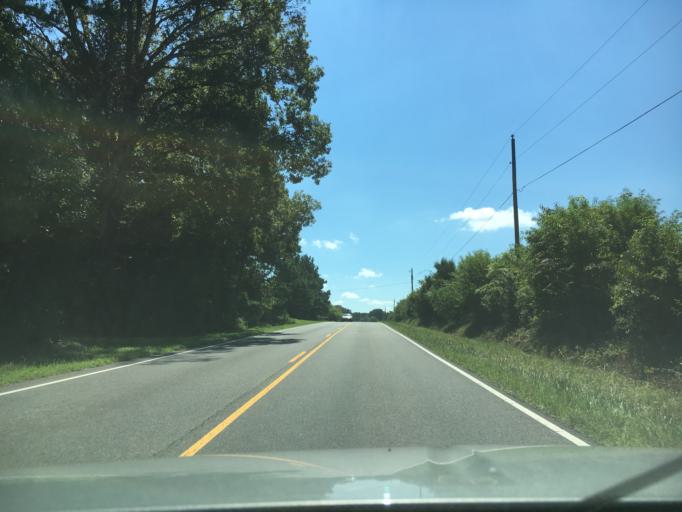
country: US
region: Virginia
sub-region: Amelia County
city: Amelia Court House
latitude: 37.4007
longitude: -77.8976
